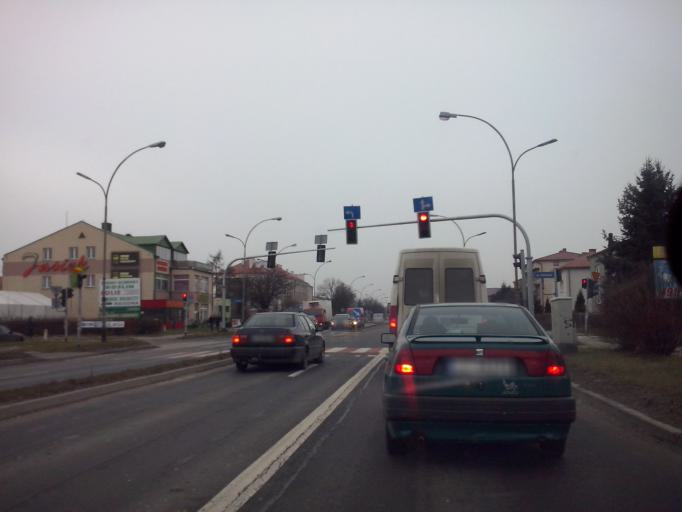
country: PL
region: Lublin Voivodeship
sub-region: Zamosc
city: Zamosc
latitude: 50.7148
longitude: 23.2261
